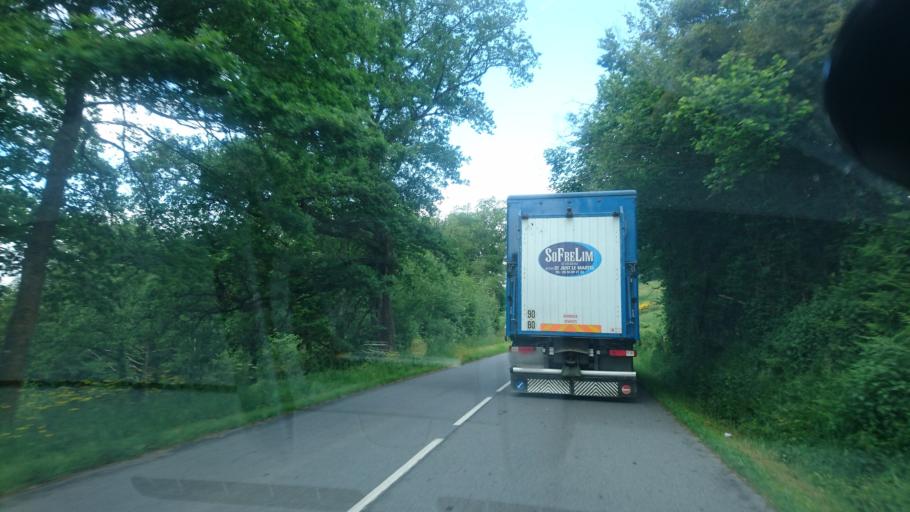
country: FR
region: Limousin
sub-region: Departement de la Haute-Vienne
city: Neuvic-Entier
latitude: 45.7176
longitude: 1.6112
